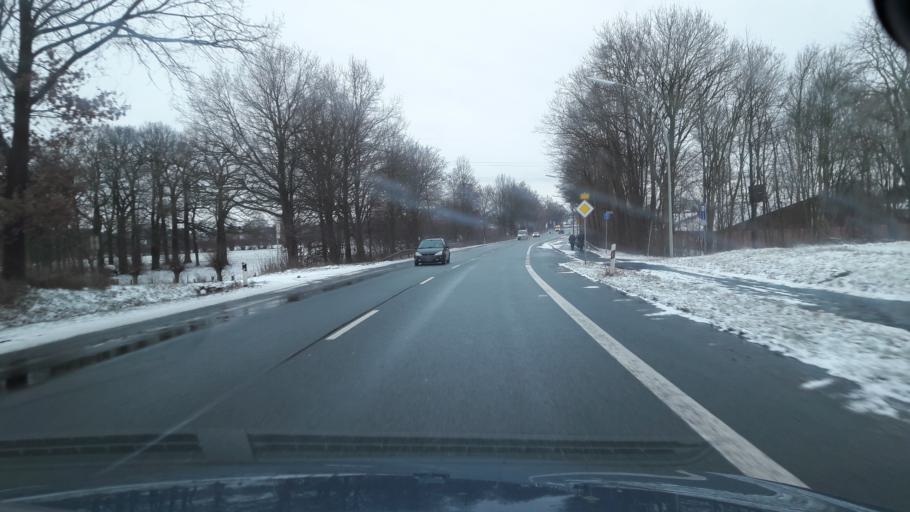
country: DE
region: North Rhine-Westphalia
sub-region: Regierungsbezirk Munster
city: Ennigerloh
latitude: 51.8110
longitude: 8.0248
